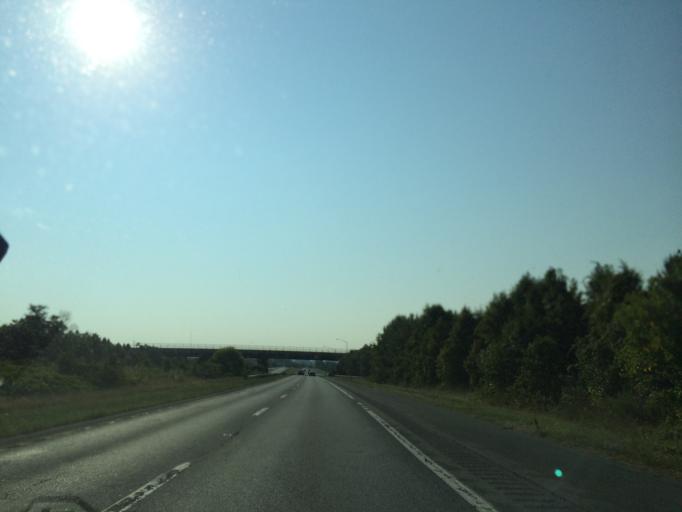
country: US
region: Maryland
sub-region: Howard County
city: Fort George G Mead Junction
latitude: 39.1293
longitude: -76.7974
